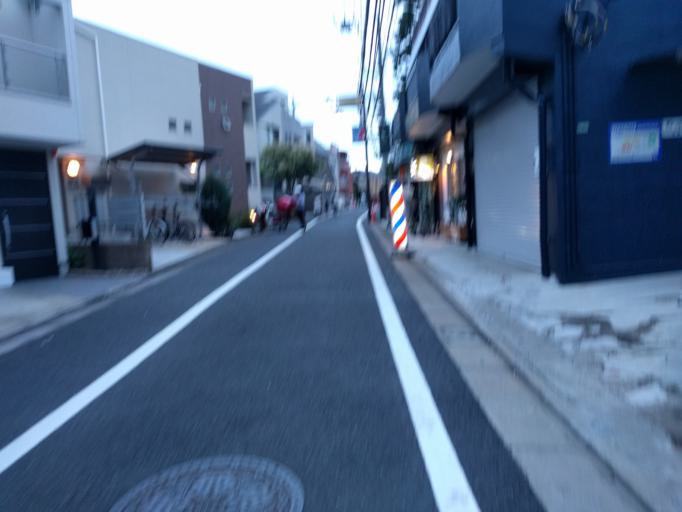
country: JP
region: Tokyo
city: Tokyo
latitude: 35.6373
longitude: 139.6685
